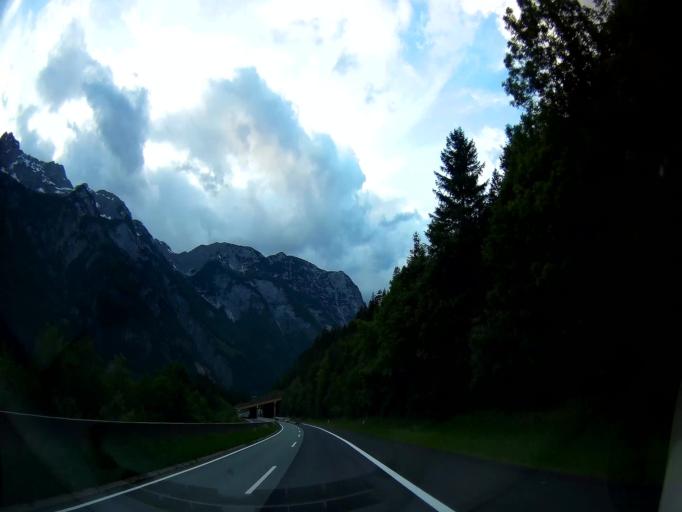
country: AT
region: Salzburg
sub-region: Politischer Bezirk Sankt Johann im Pongau
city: Werfen
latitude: 47.5039
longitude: 13.1789
